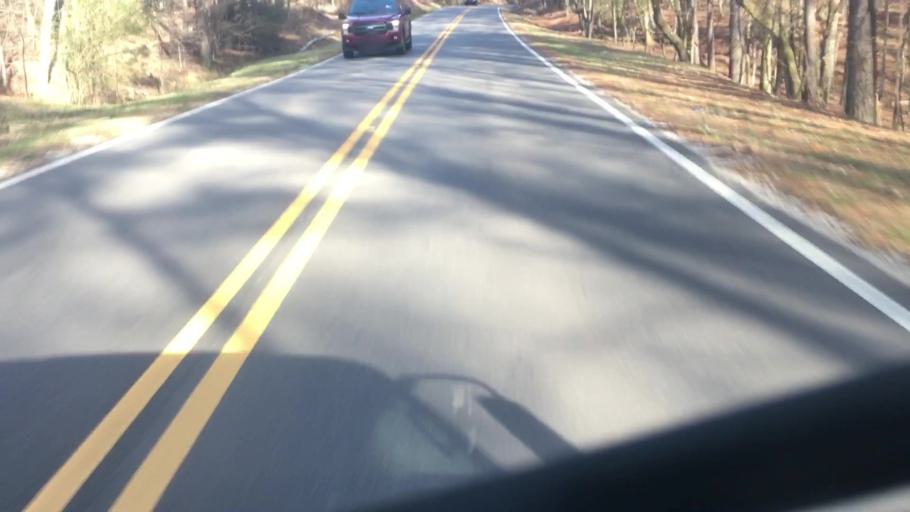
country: US
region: Alabama
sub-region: Shelby County
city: Brook Highland
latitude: 33.4554
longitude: -86.6847
